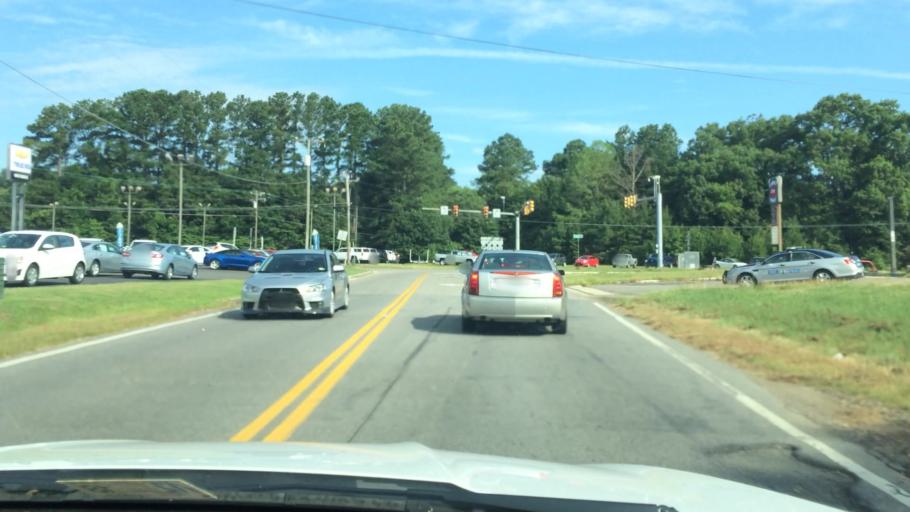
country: US
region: Virginia
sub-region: King William County
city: West Point
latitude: 37.5233
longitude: -76.8259
